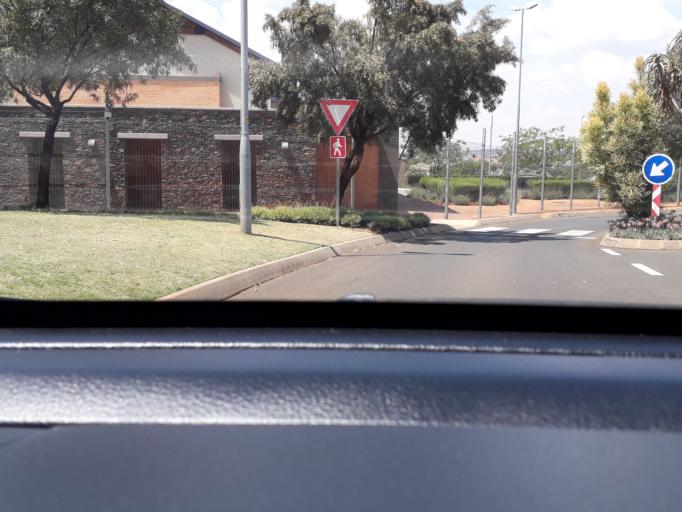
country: ZA
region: Gauteng
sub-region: City of Tshwane Metropolitan Municipality
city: Centurion
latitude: -25.9216
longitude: 28.1898
